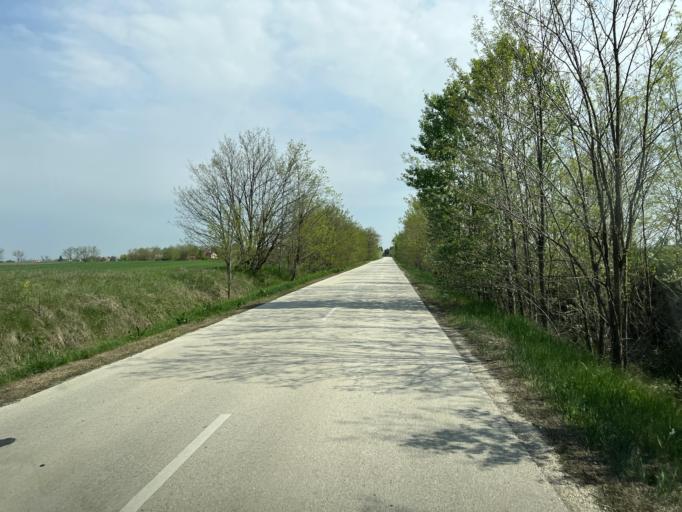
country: HU
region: Pest
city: Jaszkarajeno
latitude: 47.0880
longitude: 20.0177
